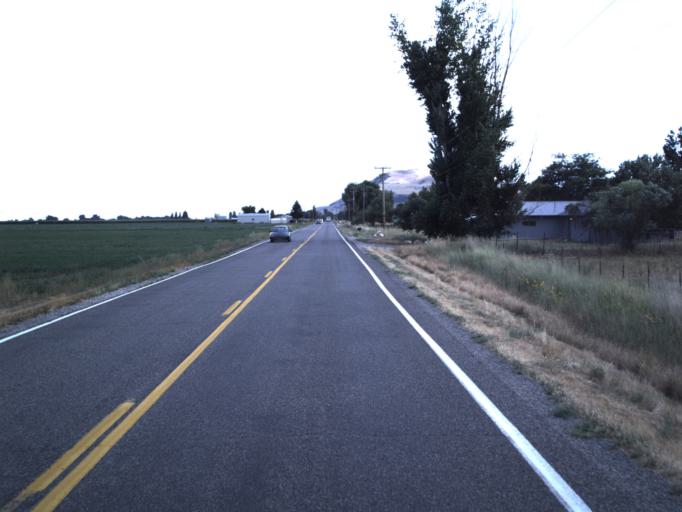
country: US
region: Utah
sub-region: Cache County
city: Lewiston
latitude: 41.9518
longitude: -111.9539
